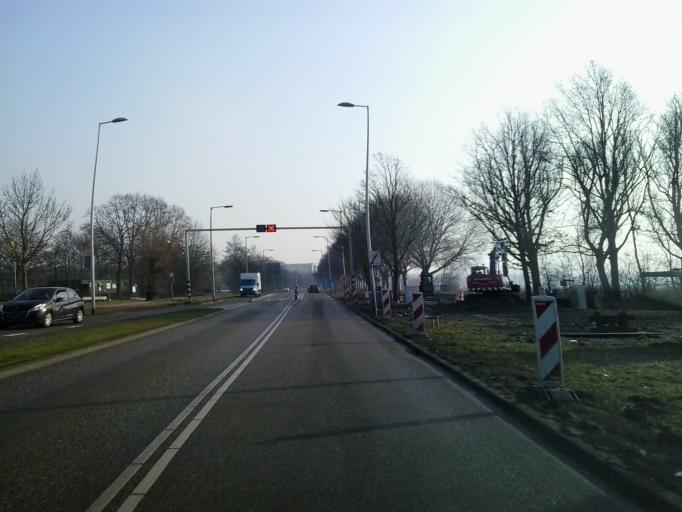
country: NL
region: South Holland
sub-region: Gemeente Capelle aan den IJssel
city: Capelle-West
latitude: 51.8861
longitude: 4.5707
